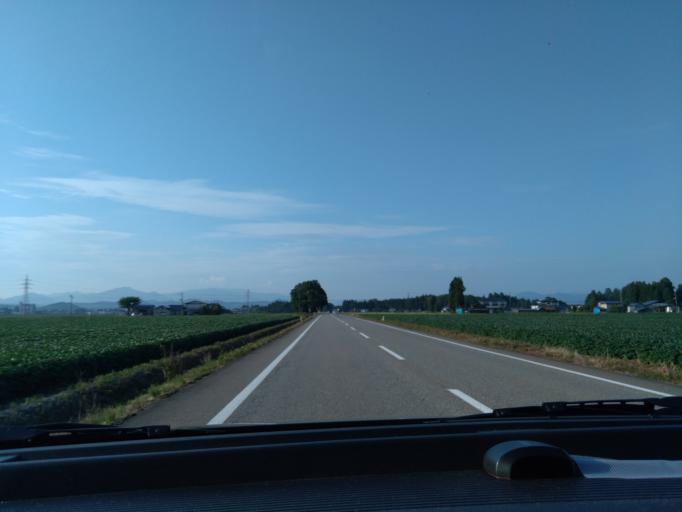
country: JP
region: Akita
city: Kakunodatemachi
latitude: 39.5323
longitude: 140.5583
